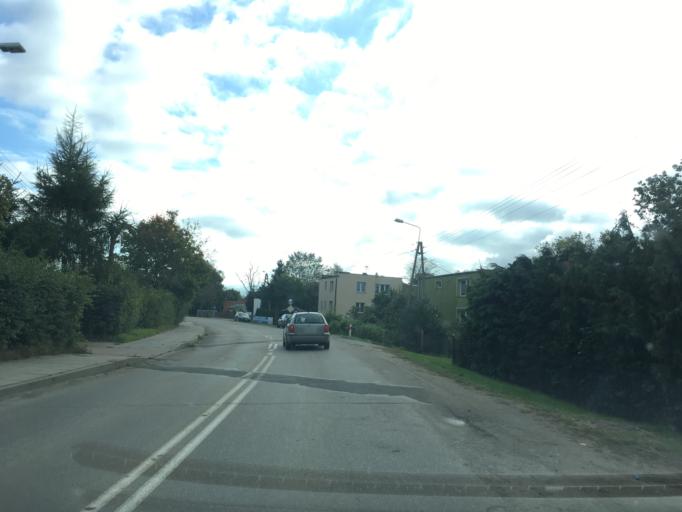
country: PL
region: Pomeranian Voivodeship
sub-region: Powiat nowodworski
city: Stegna
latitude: 54.3272
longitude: 19.1061
